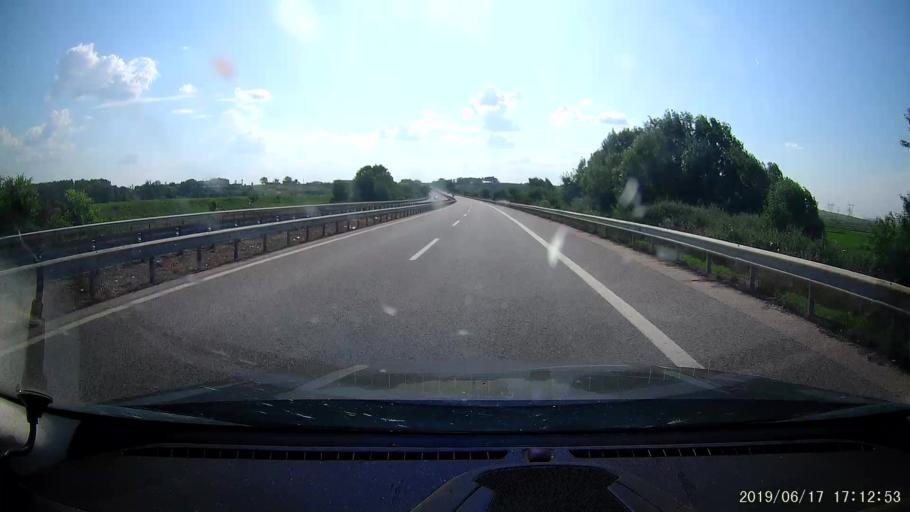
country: TR
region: Edirne
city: Edirne
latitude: 41.7013
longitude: 26.5524
